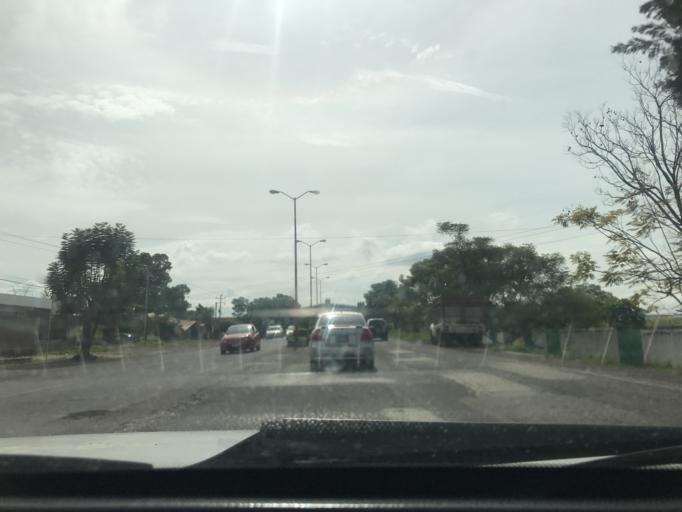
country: MX
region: Morelos
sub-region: Atlatlahucan
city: Colonia San Francisco
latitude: 18.8956
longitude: -98.9043
